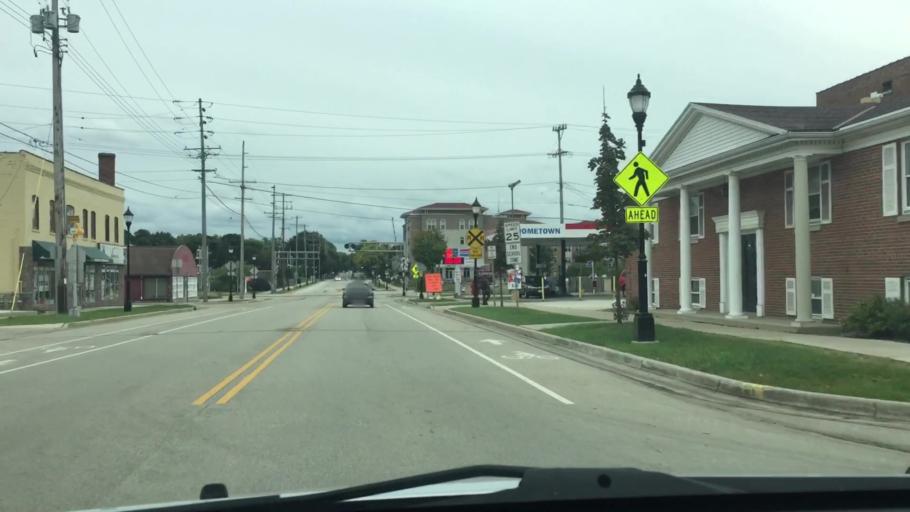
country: US
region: Wisconsin
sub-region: Waukesha County
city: Waukesha
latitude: 43.0065
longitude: -88.2318
